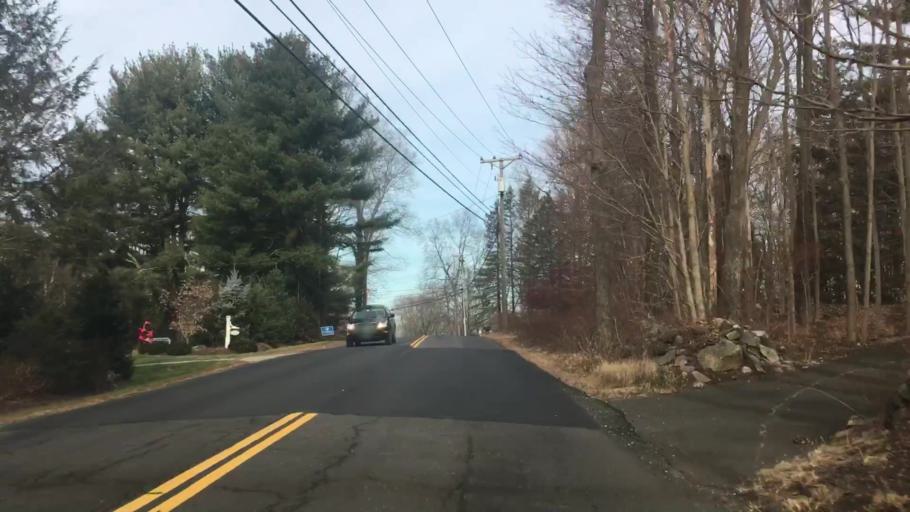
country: US
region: Connecticut
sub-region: Fairfield County
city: Newtown
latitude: 41.3956
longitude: -73.2586
